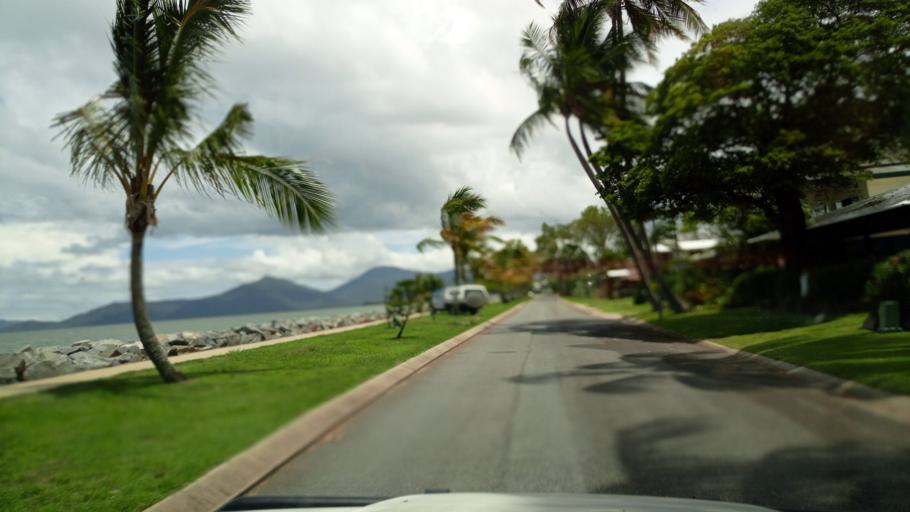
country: AU
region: Queensland
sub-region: Cairns
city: Yorkeys Knob
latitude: -16.8485
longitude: 145.7475
